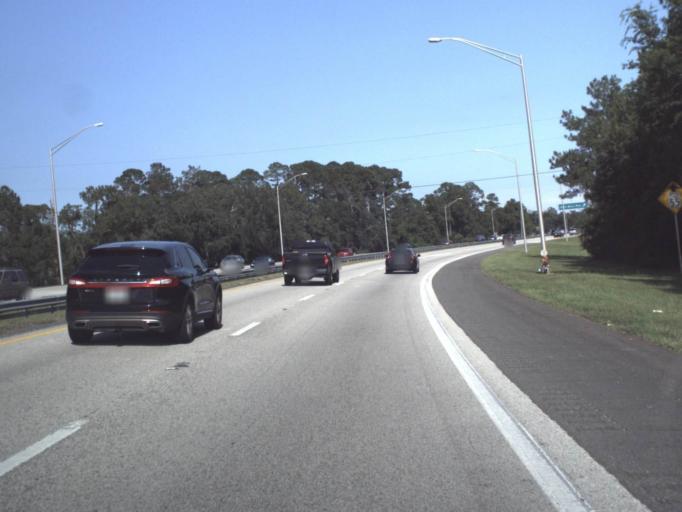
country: US
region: Florida
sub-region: Saint Johns County
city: Ponte Vedra Beach
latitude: 30.2589
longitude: -81.4068
